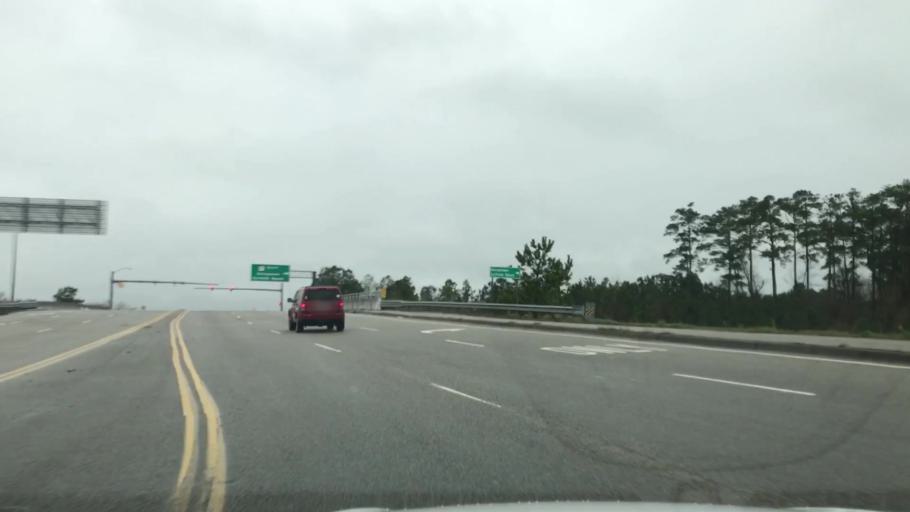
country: US
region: South Carolina
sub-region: Horry County
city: Forestbrook
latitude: 33.7030
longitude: -78.9299
